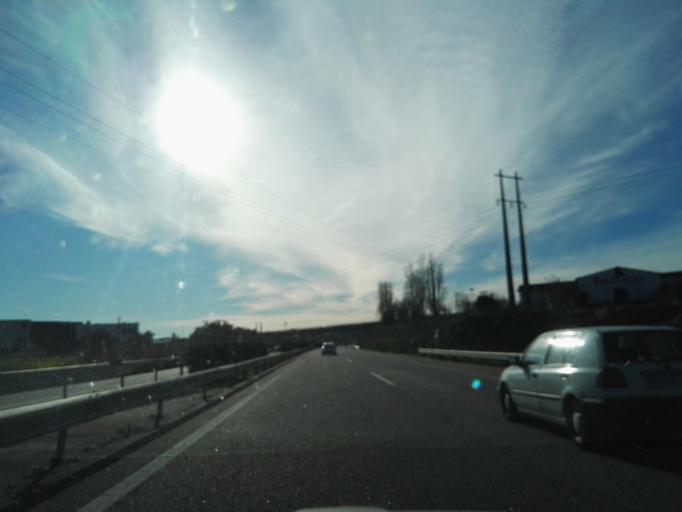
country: PT
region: Santarem
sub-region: Torres Novas
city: Torres Novas
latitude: 39.4676
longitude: -8.5217
